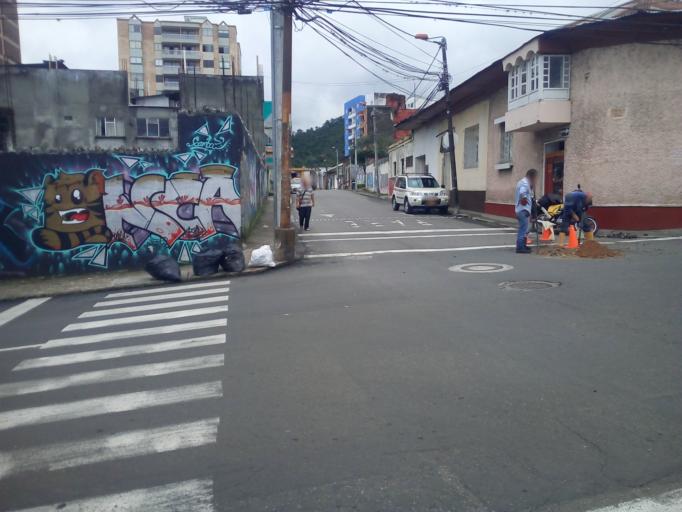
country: CO
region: Tolima
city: Ibague
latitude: 4.4474
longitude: -75.2455
